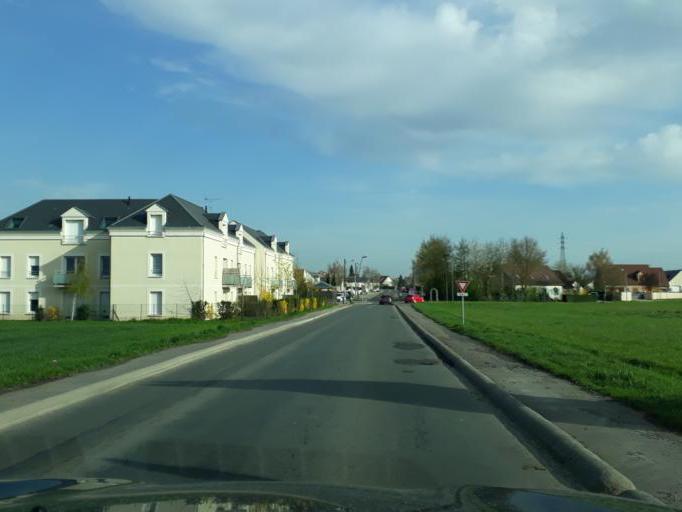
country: FR
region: Centre
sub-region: Departement du Loiret
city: La Chapelle-Saint-Mesmin
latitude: 47.9033
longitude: 1.8363
